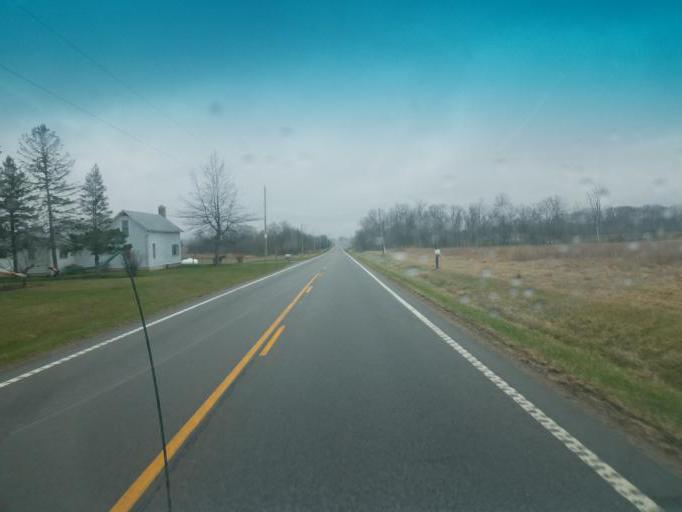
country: US
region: Ohio
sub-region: Defiance County
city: Hicksville
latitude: 41.3595
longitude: -84.7480
